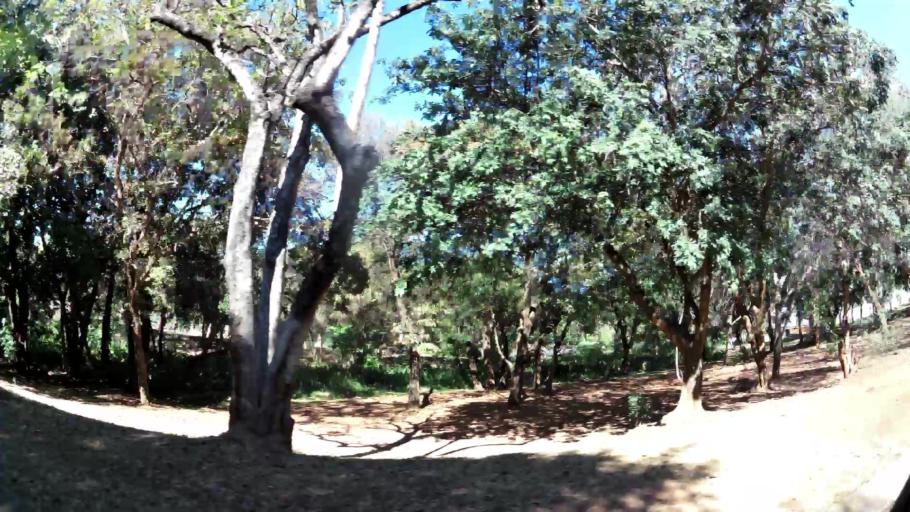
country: ZA
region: Limpopo
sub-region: Mopani District Municipality
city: Tzaneen
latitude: -23.8375
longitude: 30.1573
